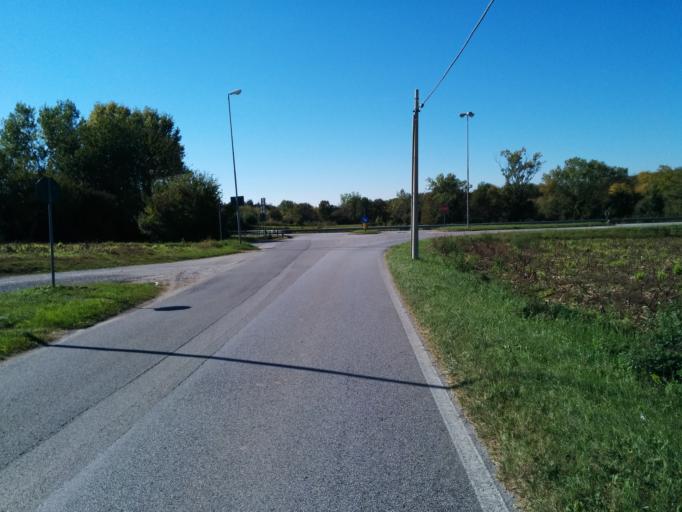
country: IT
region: Friuli Venezia Giulia
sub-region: Provincia di Udine
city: Pagnacco
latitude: 46.1133
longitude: 13.1984
